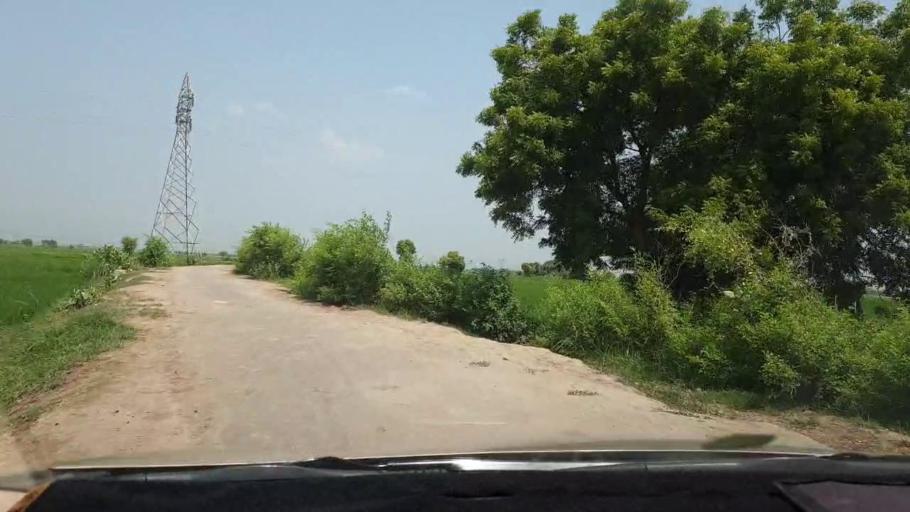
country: PK
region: Sindh
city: Naudero
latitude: 27.6635
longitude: 68.3247
